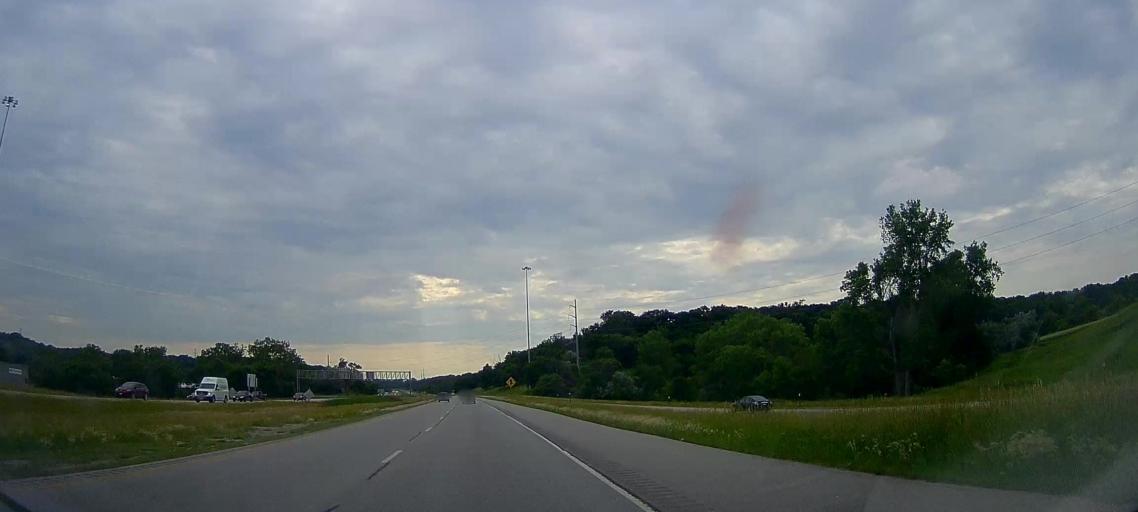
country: US
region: Iowa
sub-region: Pottawattamie County
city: Carter Lake
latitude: 41.3474
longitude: -95.9859
